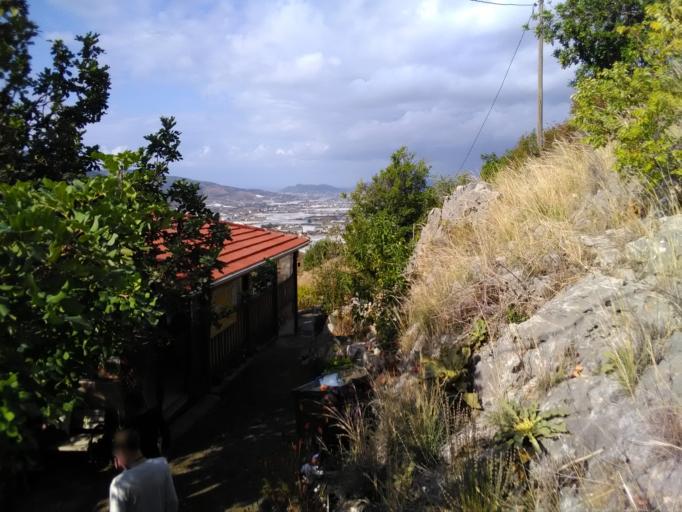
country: TR
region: Antalya
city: Gazipasa
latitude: 36.2207
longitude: 32.4023
